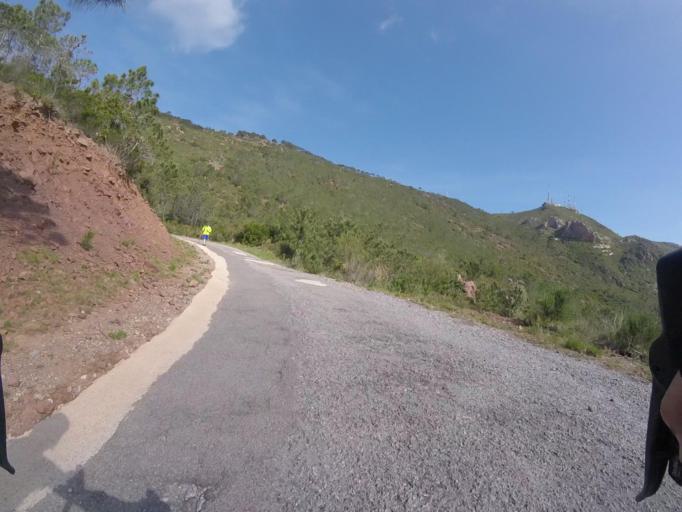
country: ES
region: Valencia
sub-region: Provincia de Castello
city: Benicassim
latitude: 40.0780
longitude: 0.0277
